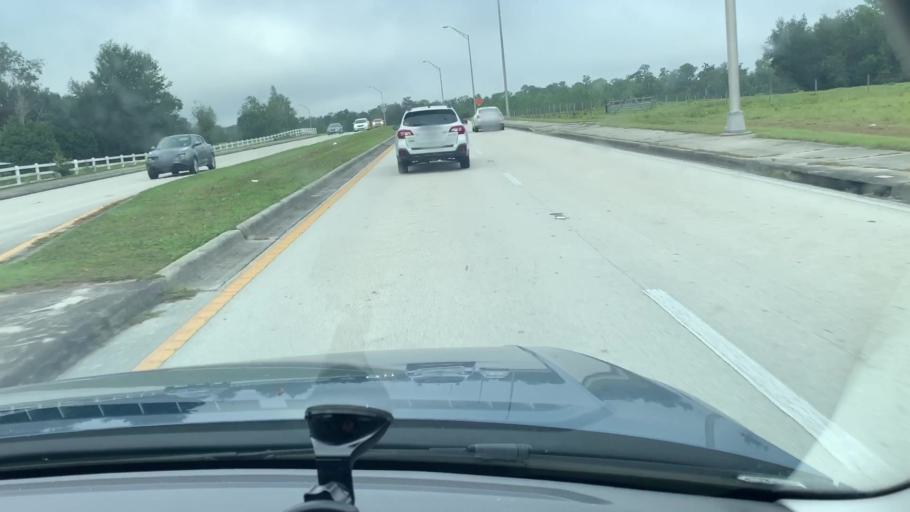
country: US
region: Florida
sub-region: Polk County
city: Kathleen
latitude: 28.0975
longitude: -82.0023
